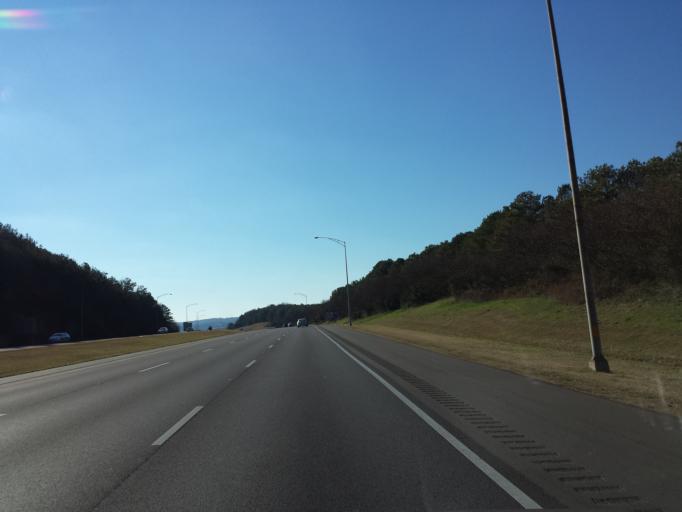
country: US
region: Alabama
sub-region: Jefferson County
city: Irondale
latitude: 33.5437
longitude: -86.6789
